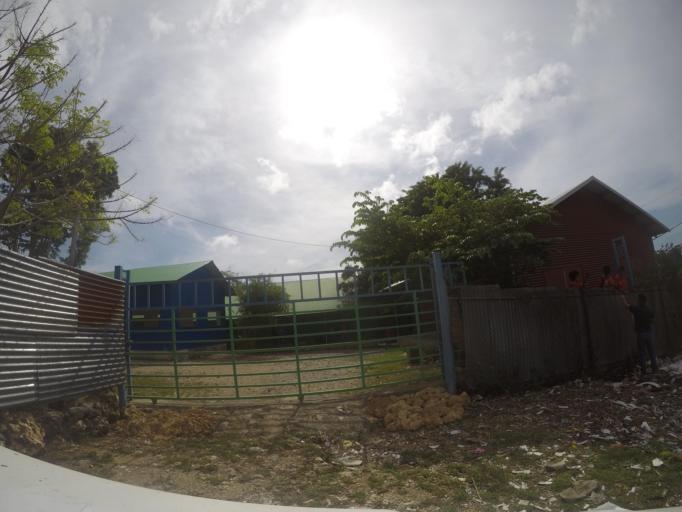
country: TL
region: Baucau
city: Baucau
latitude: -8.4805
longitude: 126.4537
